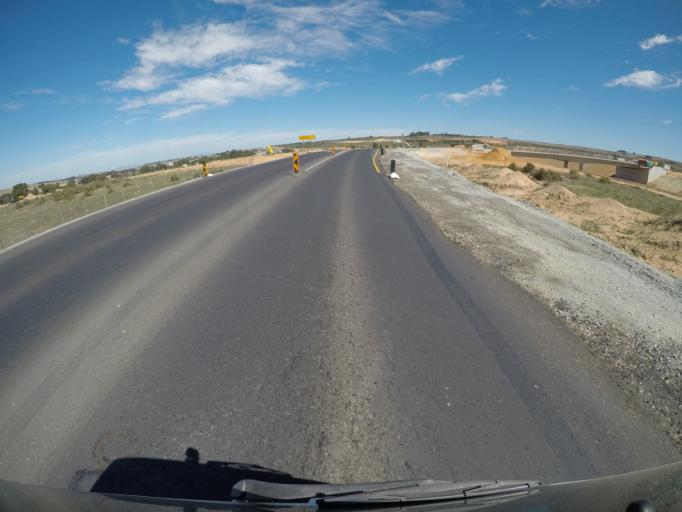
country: ZA
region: Western Cape
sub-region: West Coast District Municipality
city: Malmesbury
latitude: -33.4809
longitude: 18.6799
